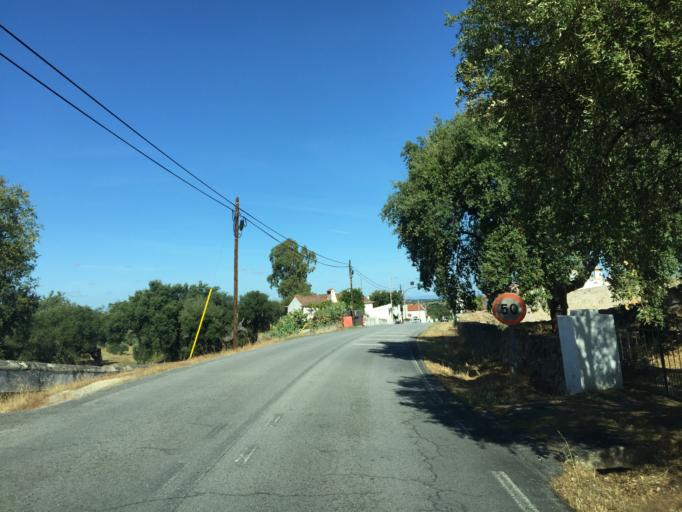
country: PT
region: Portalegre
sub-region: Marvao
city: Marvao
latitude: 39.4330
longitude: -7.3623
